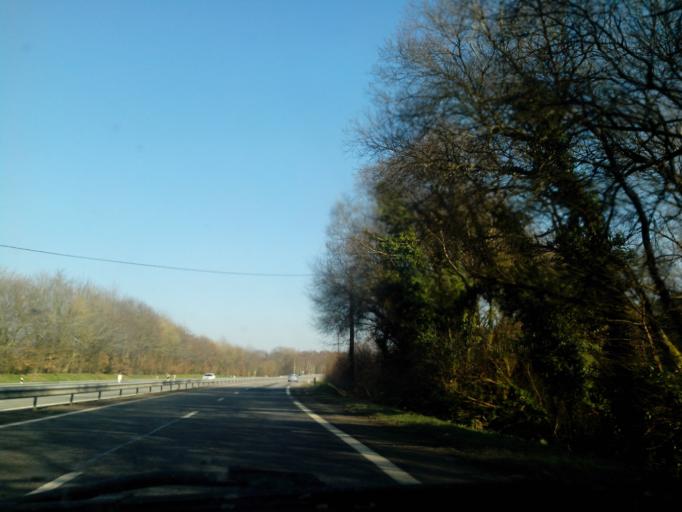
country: FR
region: Brittany
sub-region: Departement du Morbihan
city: Meneac
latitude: 48.1966
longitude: -2.5013
